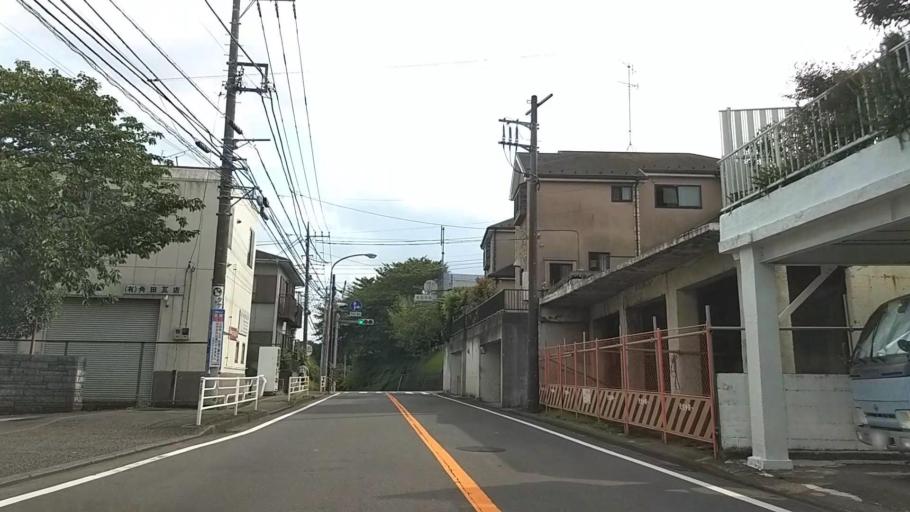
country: JP
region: Kanagawa
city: Yokohama
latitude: 35.4936
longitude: 139.5876
